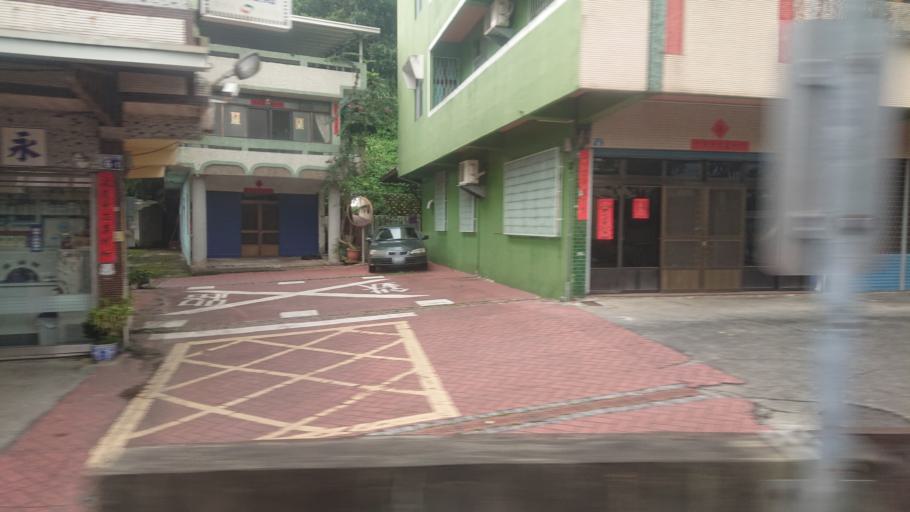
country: TW
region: Taiwan
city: Lugu
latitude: 23.8348
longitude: 120.7511
